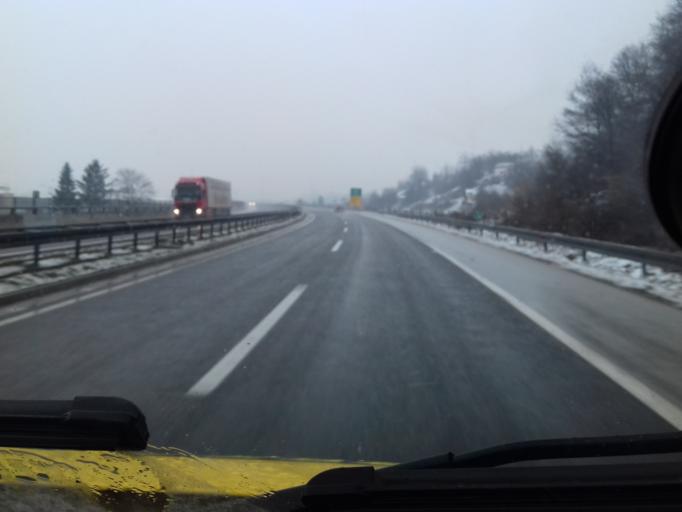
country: BA
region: Federation of Bosnia and Herzegovina
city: Visoko
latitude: 44.0019
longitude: 18.1795
